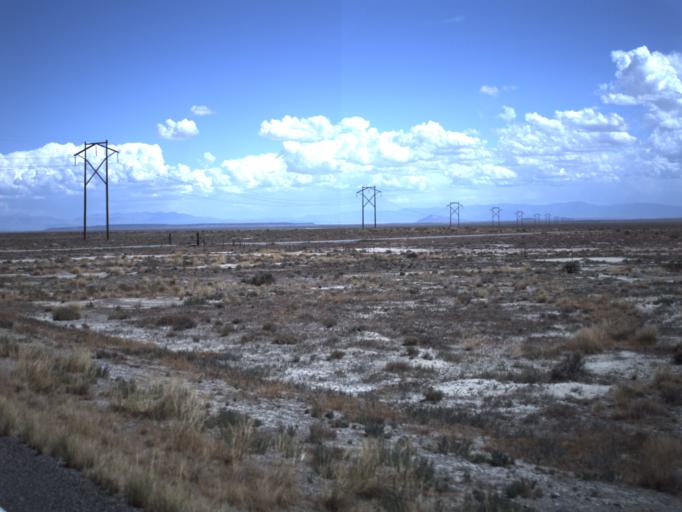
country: US
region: Utah
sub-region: Millard County
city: Delta
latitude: 39.1723
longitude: -113.0313
